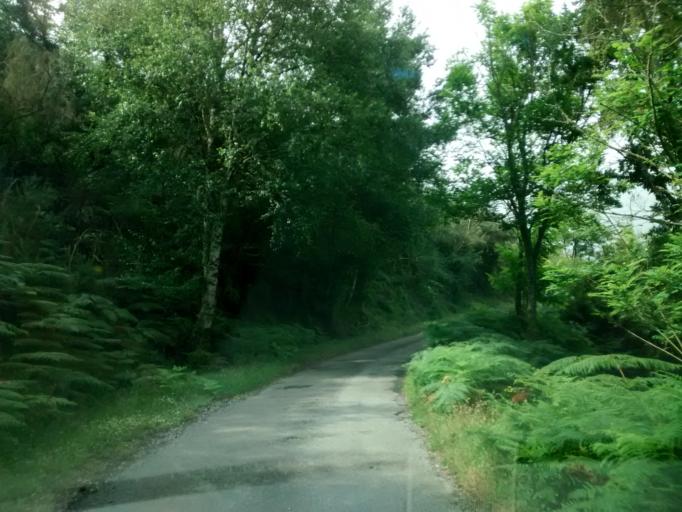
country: ES
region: Galicia
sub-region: Provincia de Ourense
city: Castro Caldelas
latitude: 42.4230
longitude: -7.3863
